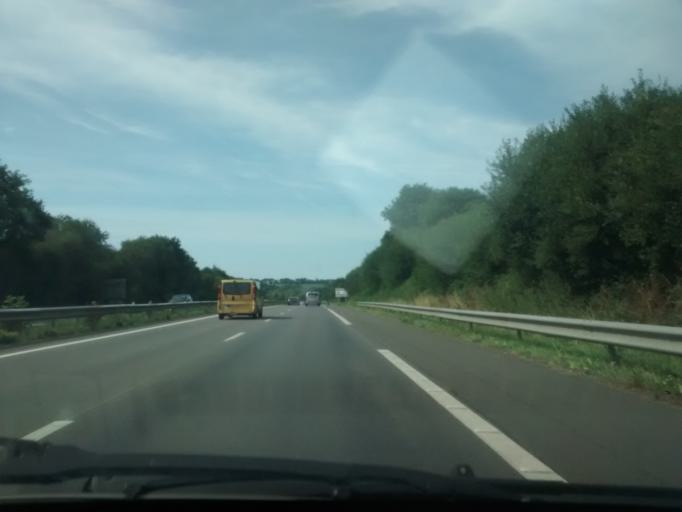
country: FR
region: Brittany
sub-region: Departement d'Ille-et-Vilaine
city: Quedillac
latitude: 48.2599
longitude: -2.1433
